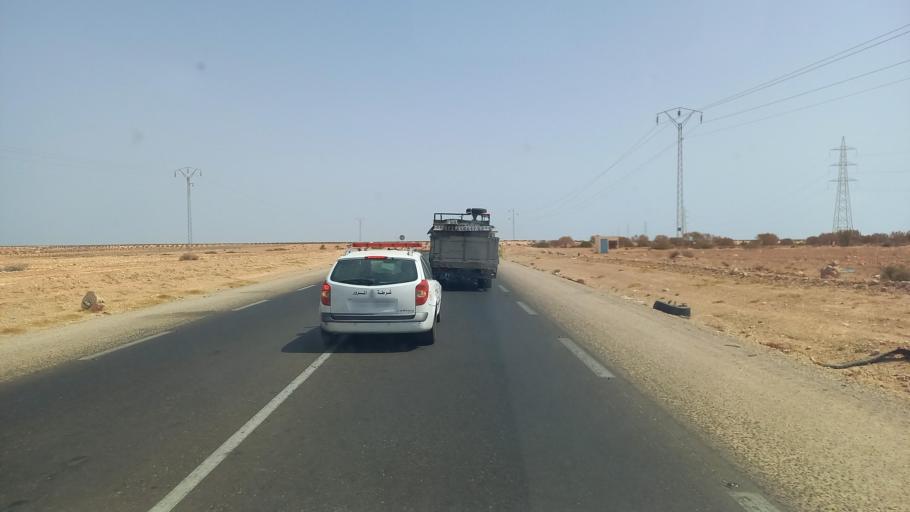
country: TN
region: Madanin
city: Zarzis
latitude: 33.4064
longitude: 10.8591
